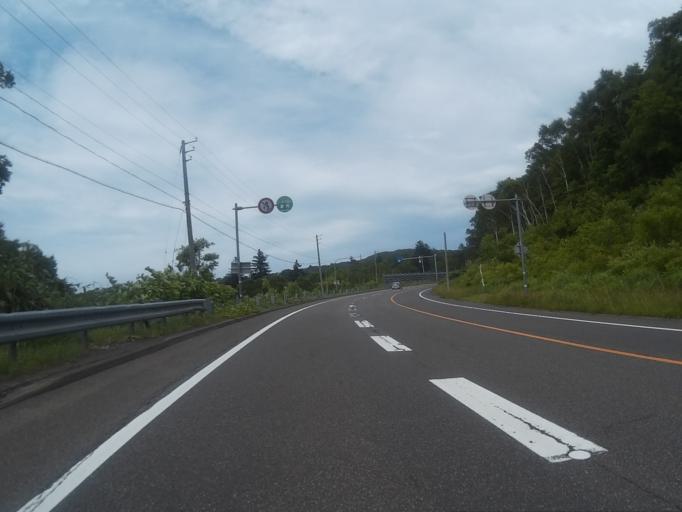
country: JP
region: Hokkaido
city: Sapporo
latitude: 42.8526
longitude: 141.0916
